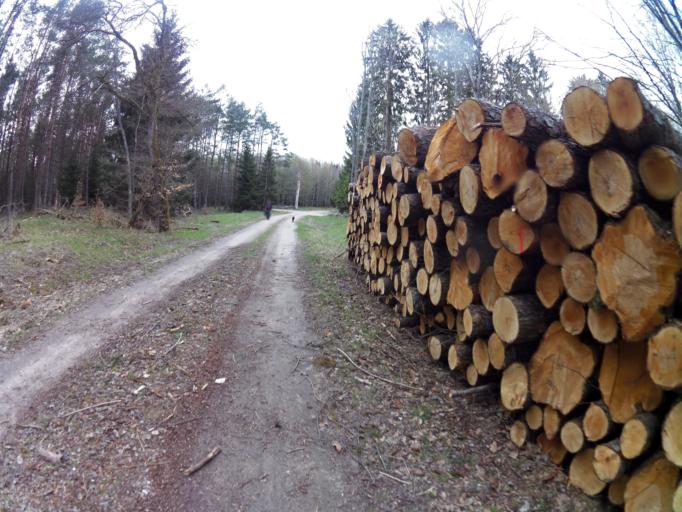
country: PL
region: West Pomeranian Voivodeship
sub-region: Powiat szczecinecki
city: Bialy Bor
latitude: 53.8867
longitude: 16.7184
